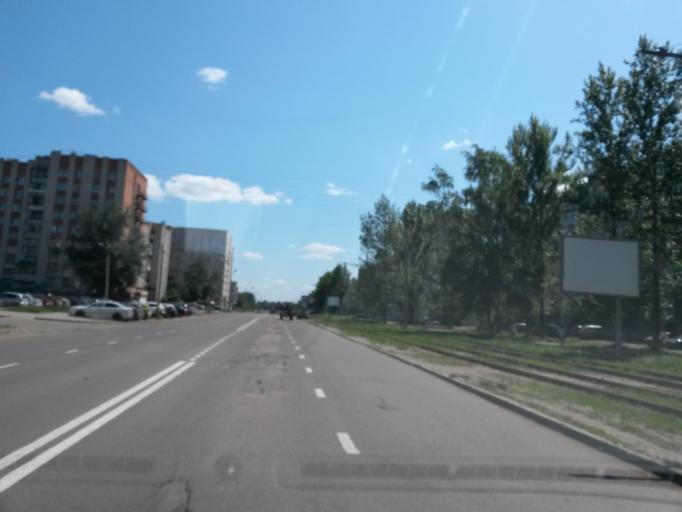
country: RU
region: Jaroslavl
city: Yaroslavl
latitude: 57.6890
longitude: 39.7612
